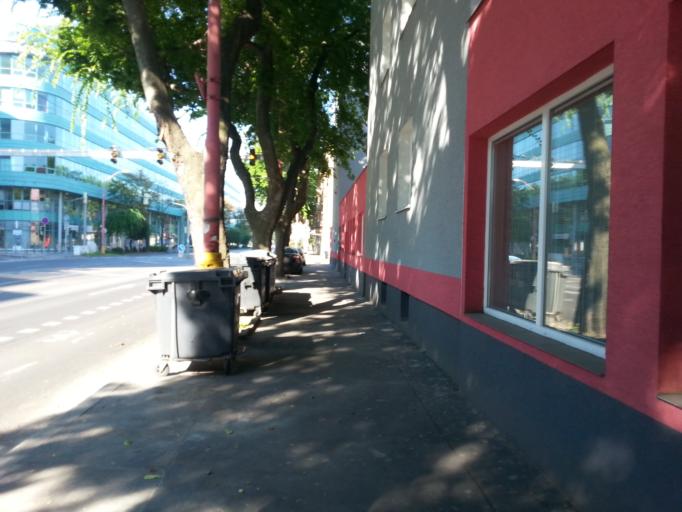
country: SK
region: Bratislavsky
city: Bratislava
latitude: 48.1466
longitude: 17.1388
